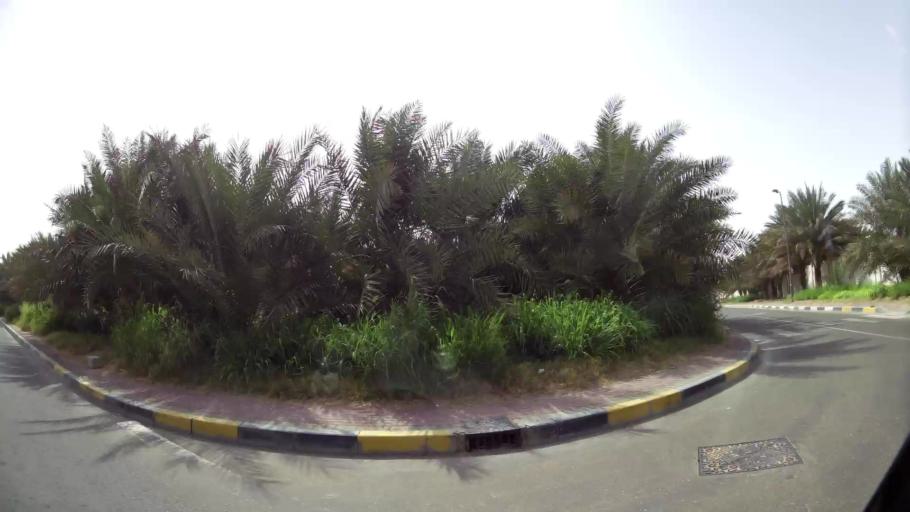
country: AE
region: Abu Dhabi
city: Al Ain
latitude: 24.1683
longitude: 55.6993
